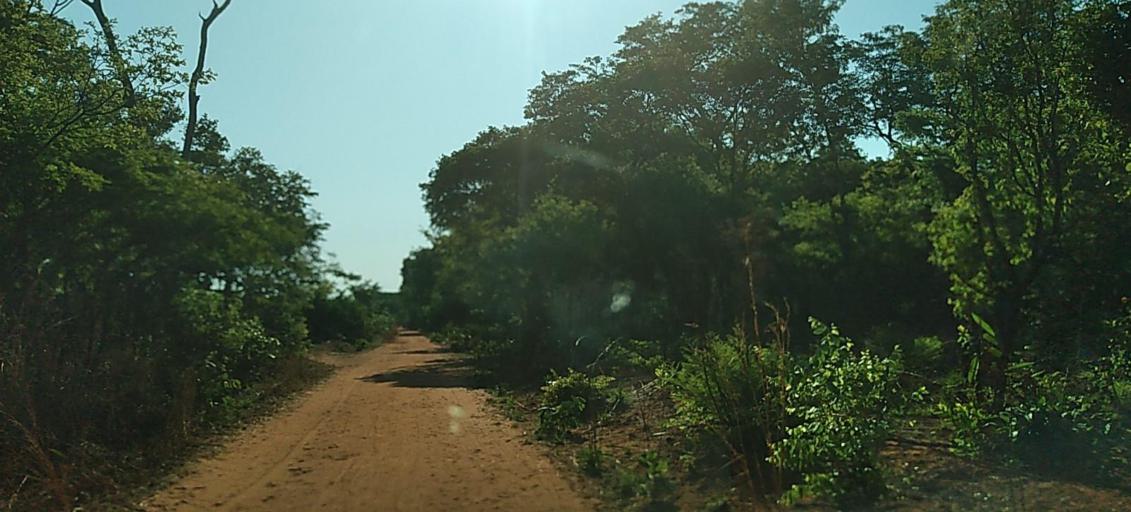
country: ZM
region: Copperbelt
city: Luanshya
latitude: -13.4589
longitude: 28.8231
